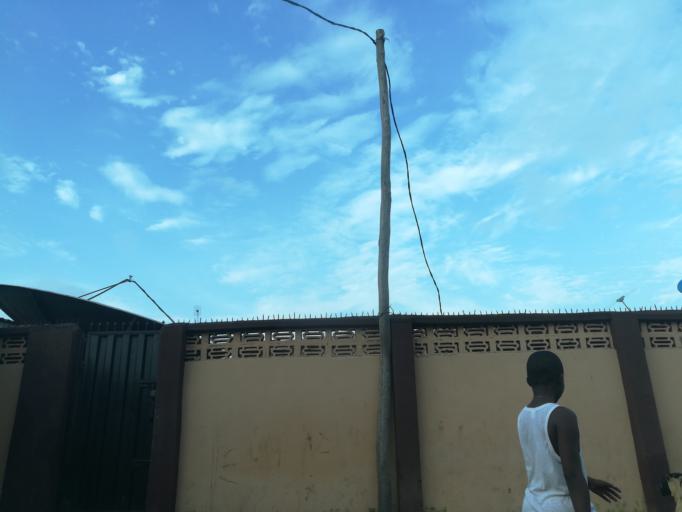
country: NG
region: Lagos
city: Ebute Ikorodu
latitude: 6.6142
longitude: 3.4749
